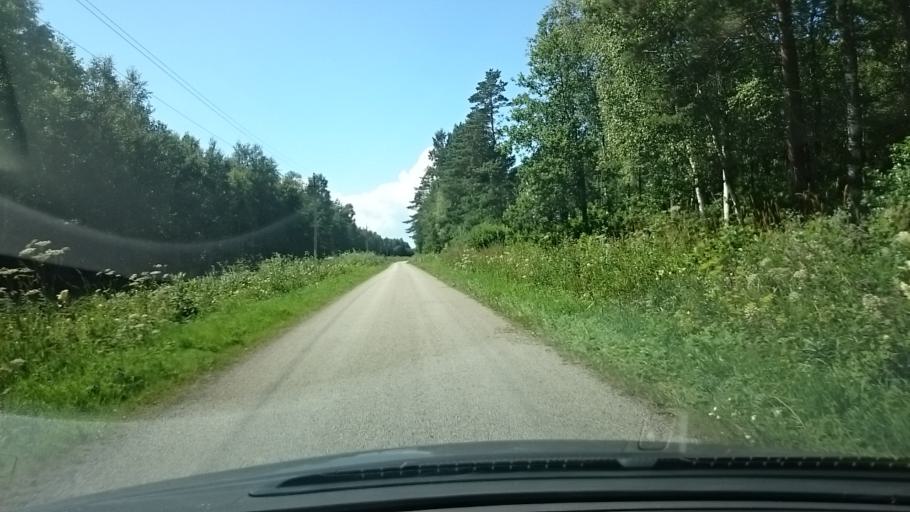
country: EE
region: Laeaene
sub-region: Haapsalu linn
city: Haapsalu
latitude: 59.0107
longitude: 23.5477
